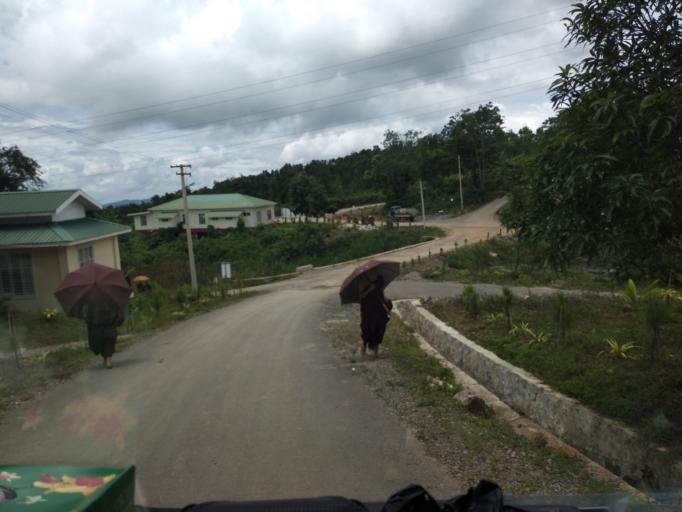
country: MM
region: Mandalay
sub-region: Pyin Oo Lwin District
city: Pyin Oo Lwin
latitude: 21.9109
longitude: 96.3838
